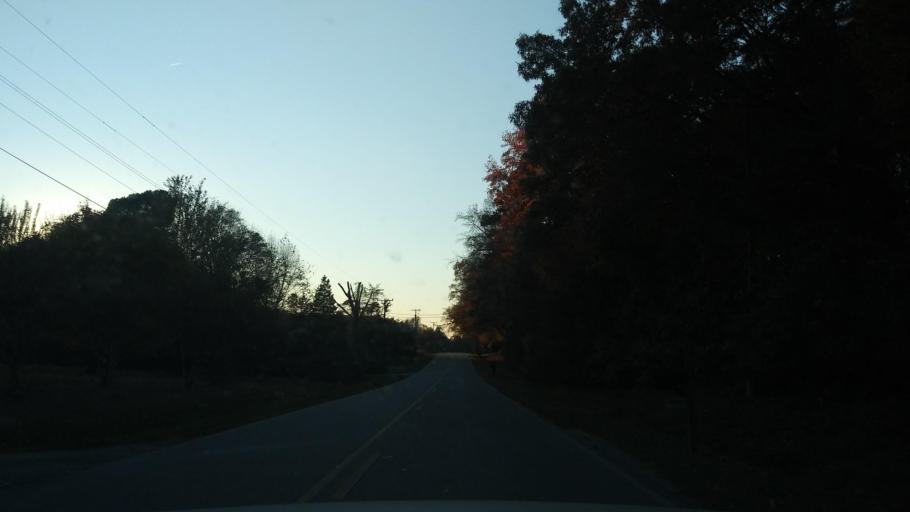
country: US
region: North Carolina
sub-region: Guilford County
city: Pleasant Garden
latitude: 36.0013
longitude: -79.7646
